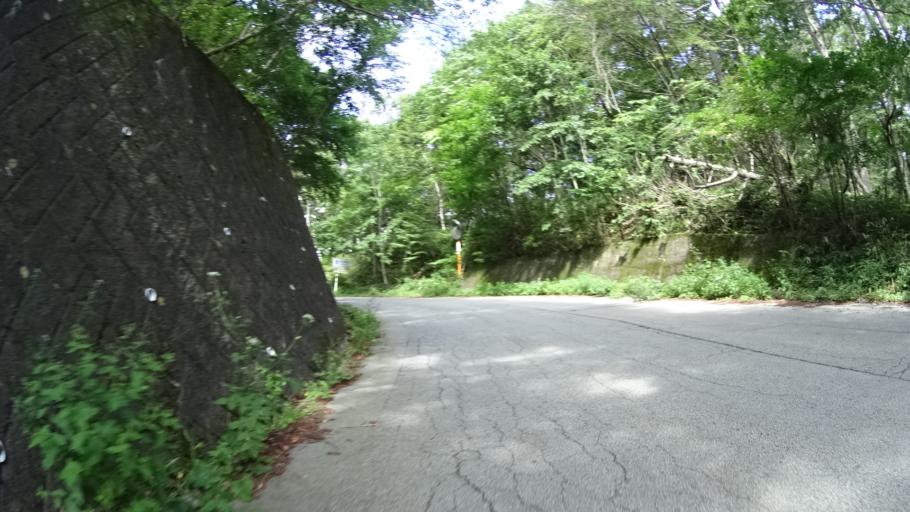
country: JP
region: Yamanashi
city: Nirasaki
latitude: 35.9146
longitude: 138.5424
